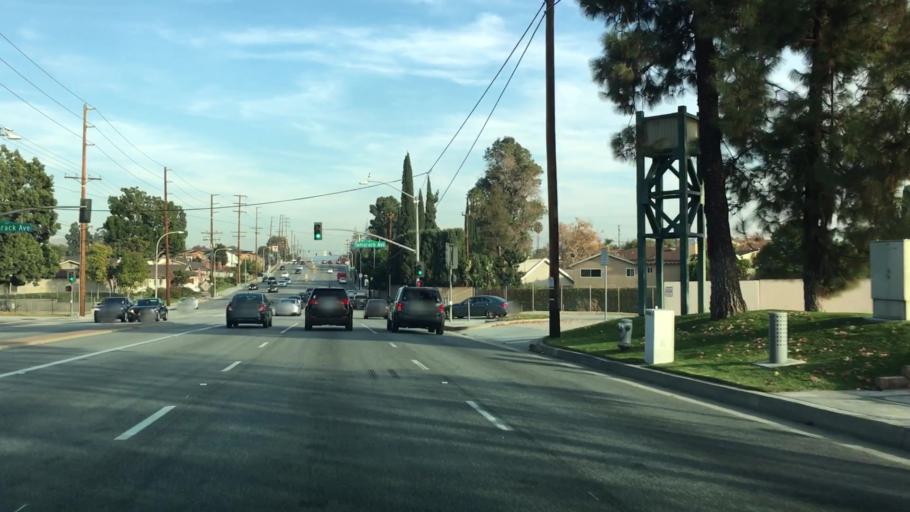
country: US
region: California
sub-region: Orange County
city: Brea
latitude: 33.9246
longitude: -117.9009
